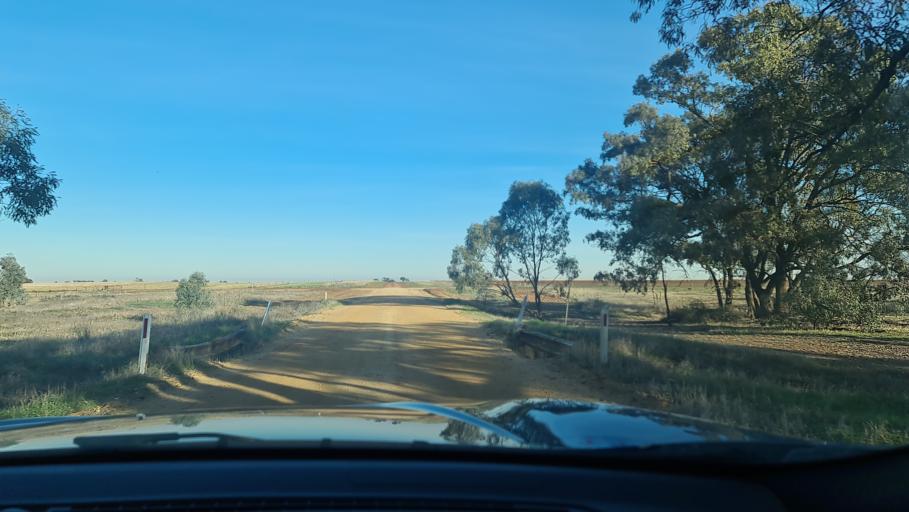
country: AU
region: Victoria
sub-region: Horsham
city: Horsham
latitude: -36.3538
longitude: 142.3960
